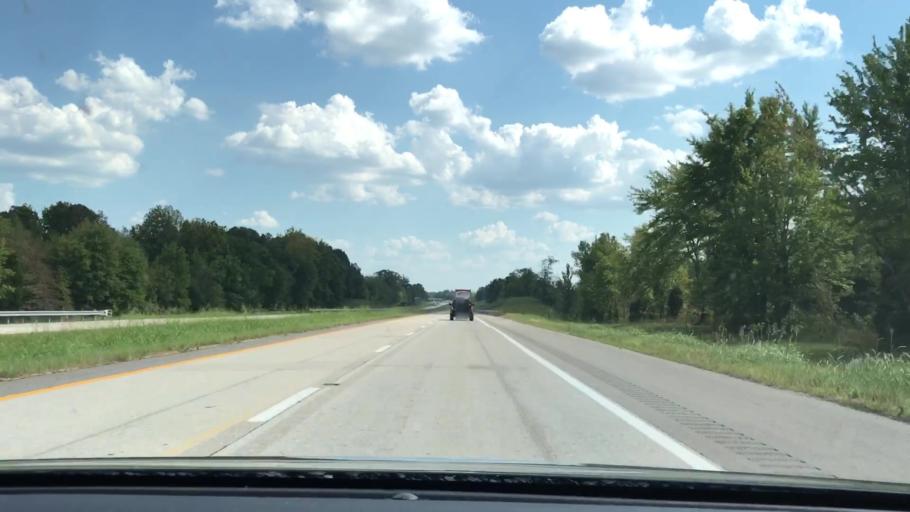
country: US
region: Kentucky
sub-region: Ohio County
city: Oak Grove
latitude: 37.3634
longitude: -86.7957
